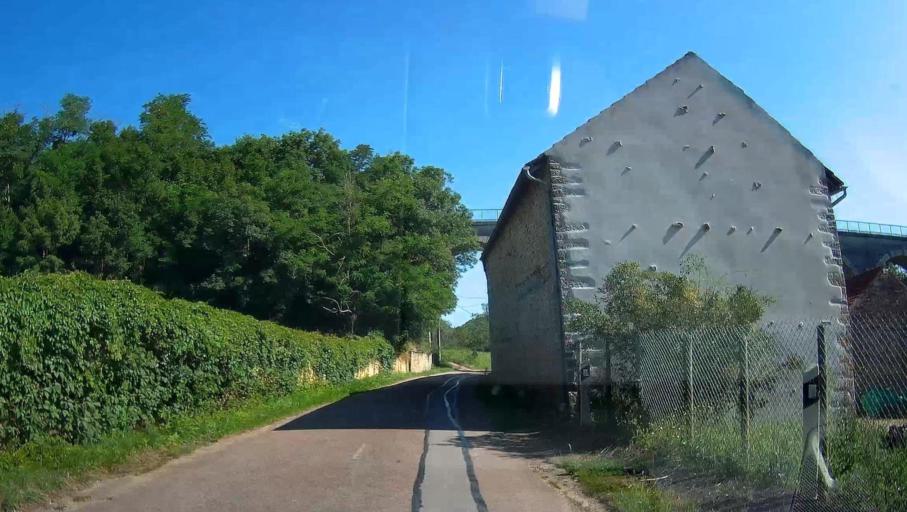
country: FR
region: Bourgogne
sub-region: Departement de la Cote-d'Or
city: Nolay
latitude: 46.9574
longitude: 4.6391
